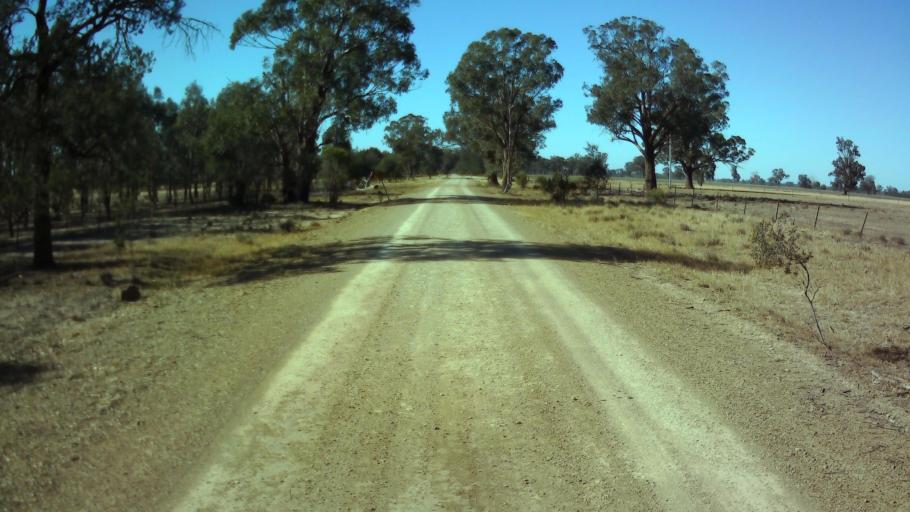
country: AU
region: New South Wales
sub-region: Weddin
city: Grenfell
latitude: -33.9306
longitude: 147.8729
